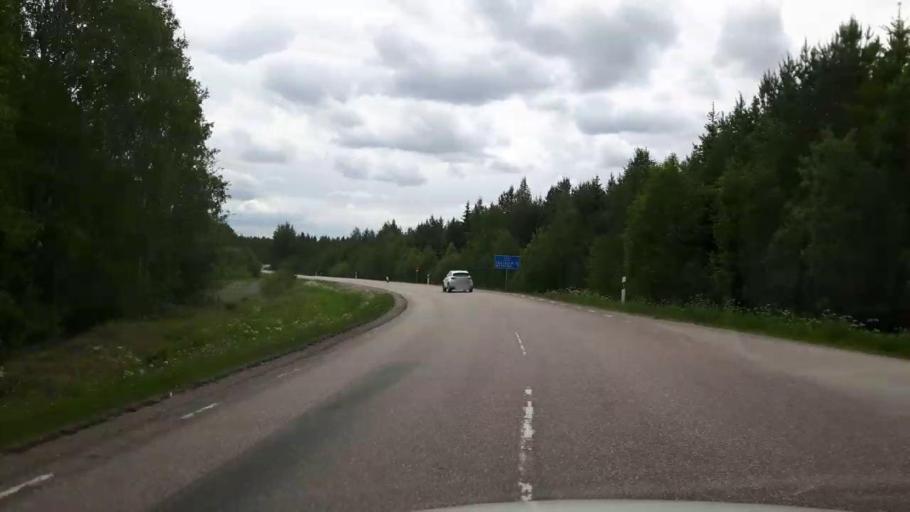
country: SE
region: Vaestmanland
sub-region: Norbergs Kommun
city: Norberg
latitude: 60.1256
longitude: 15.9178
